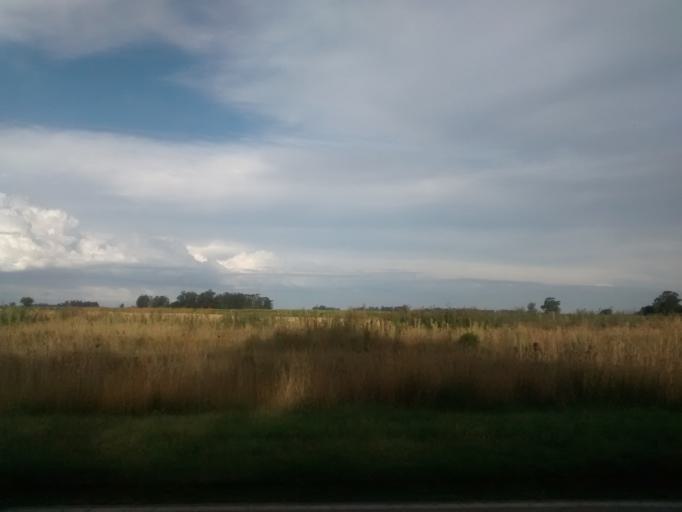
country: AR
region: Buenos Aires
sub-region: Partido de Loberia
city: Loberia
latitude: -38.2109
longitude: -58.7335
